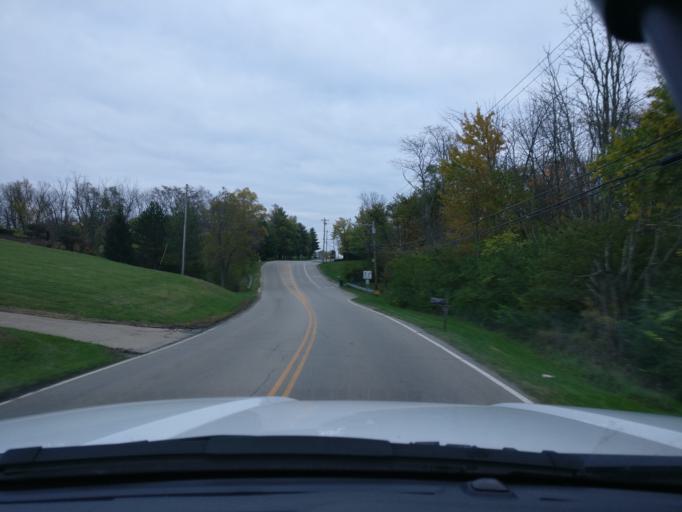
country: US
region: Ohio
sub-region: Warren County
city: Hunter
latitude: 39.4638
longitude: -84.3024
